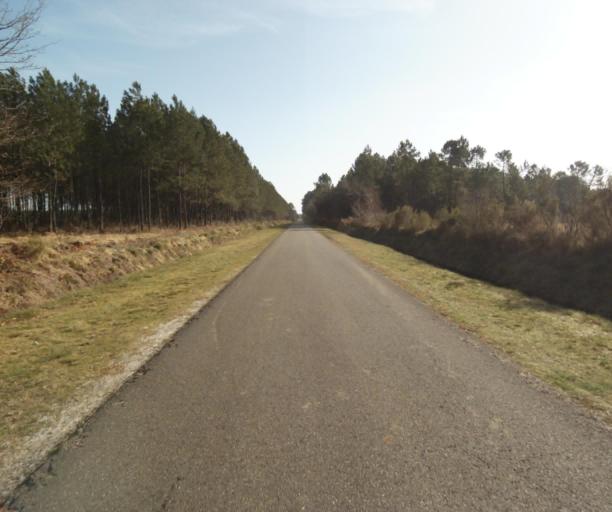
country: FR
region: Aquitaine
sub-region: Departement de la Gironde
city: Grignols
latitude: 44.2271
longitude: -0.1488
